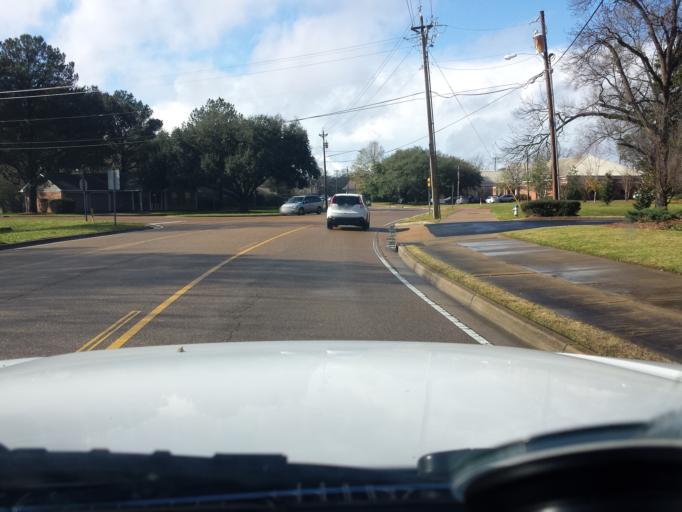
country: US
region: Mississippi
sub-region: Madison County
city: Madison
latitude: 32.4576
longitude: -90.1102
